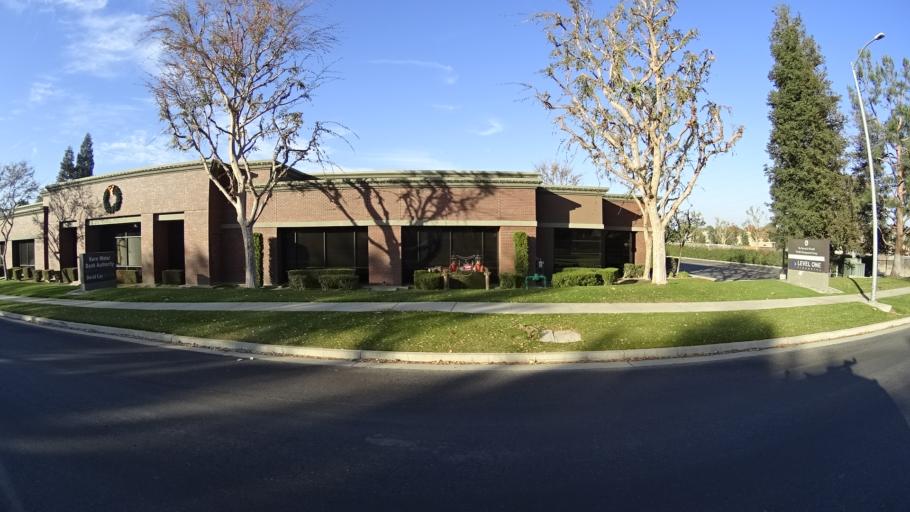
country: US
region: California
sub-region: Kern County
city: Greenacres
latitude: 35.3398
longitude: -119.0971
